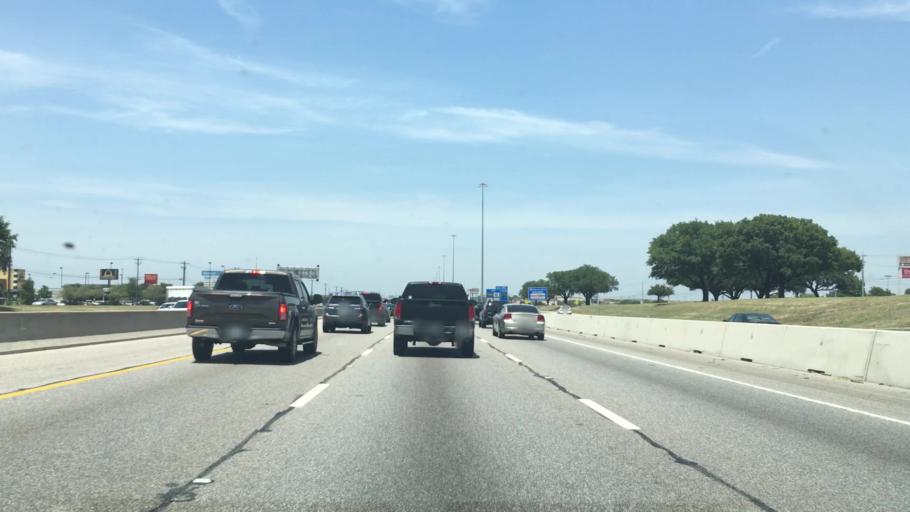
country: US
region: Texas
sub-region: Travis County
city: Wells Branch
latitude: 30.4092
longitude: -97.6743
